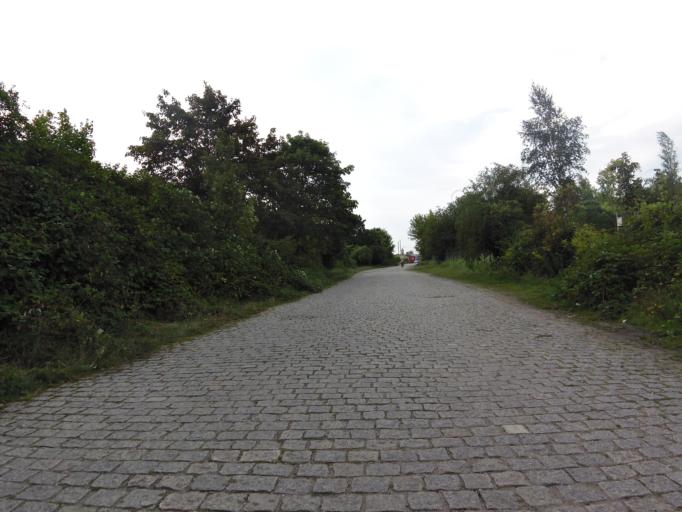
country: DE
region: Saxony
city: Leipzig
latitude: 51.3171
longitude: 12.3213
